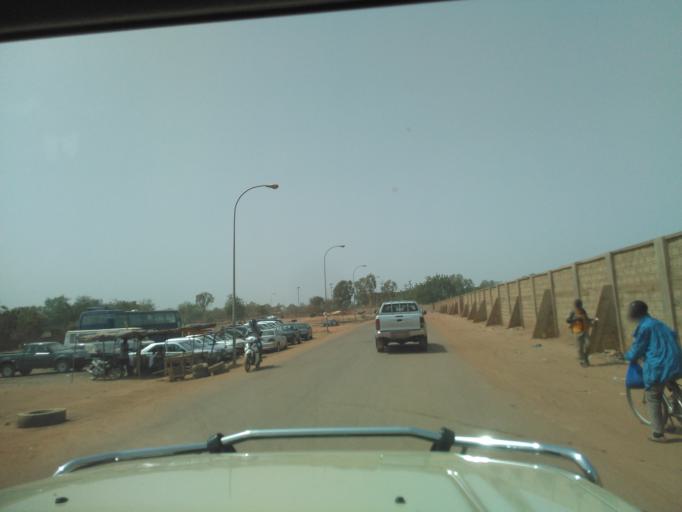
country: BF
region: Centre
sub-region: Kadiogo Province
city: Ouagadougou
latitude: 12.3969
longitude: -1.5575
